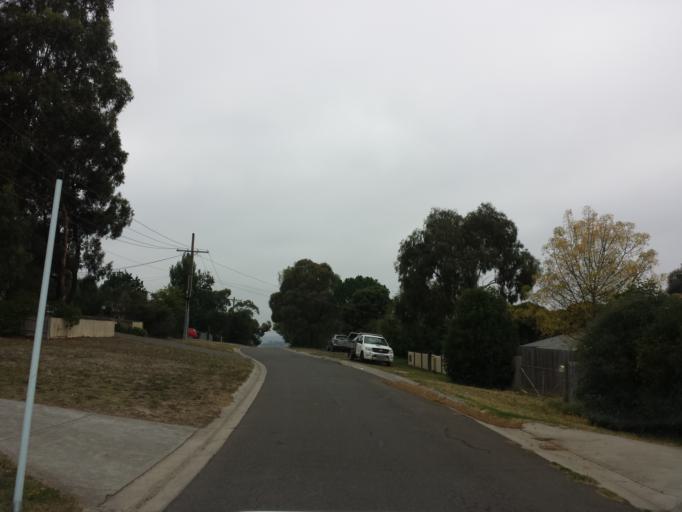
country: AU
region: Victoria
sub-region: Yarra Ranges
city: Yarra Glen
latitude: -37.6525
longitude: 145.3795
